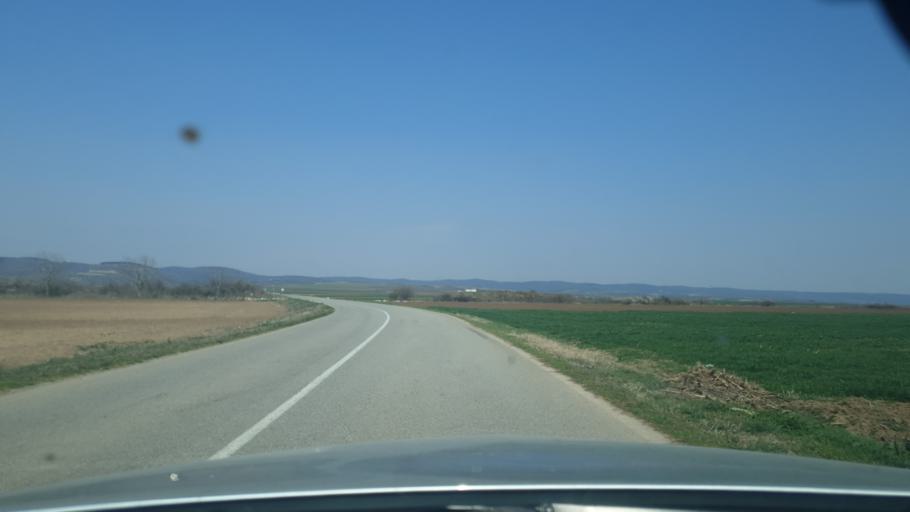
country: RS
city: Vrdnik
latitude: 45.0670
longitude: 19.7694
